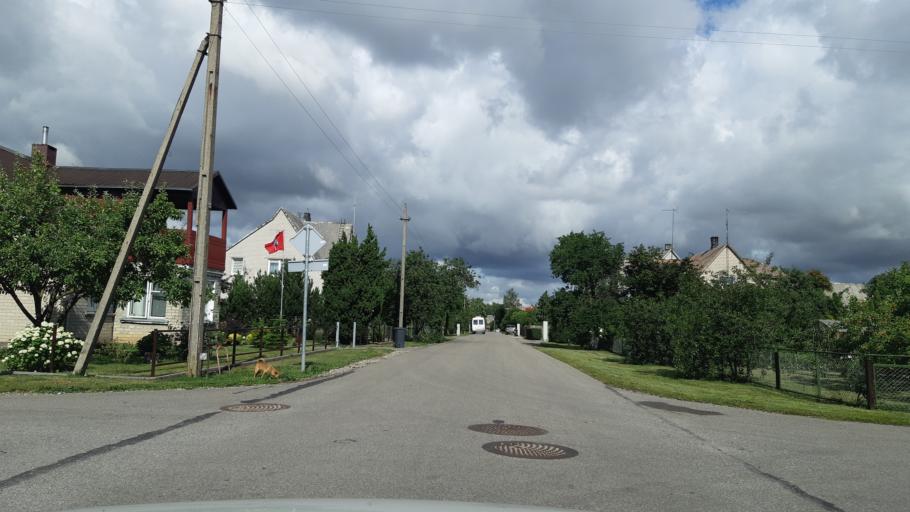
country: LT
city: Vilkaviskis
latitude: 54.6397
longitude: 23.0532
